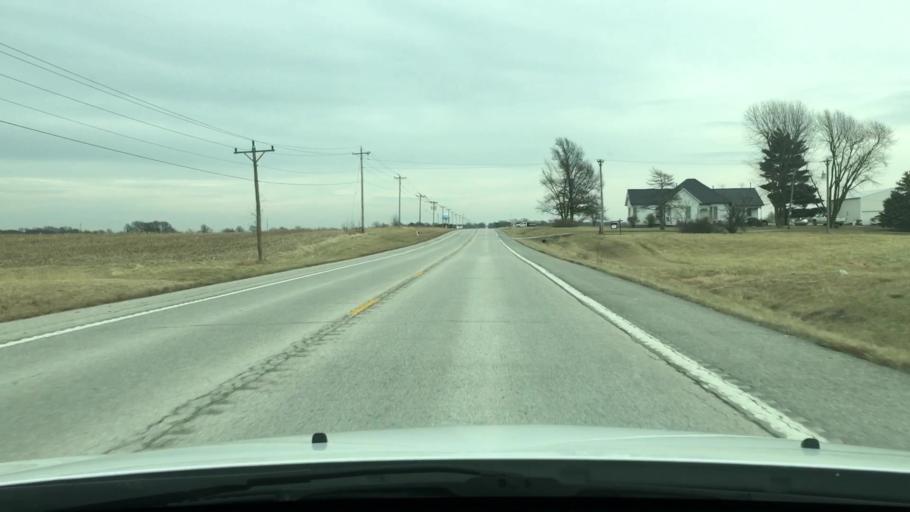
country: US
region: Missouri
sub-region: Audrain County
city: Vandalia
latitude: 39.3459
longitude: -91.3671
